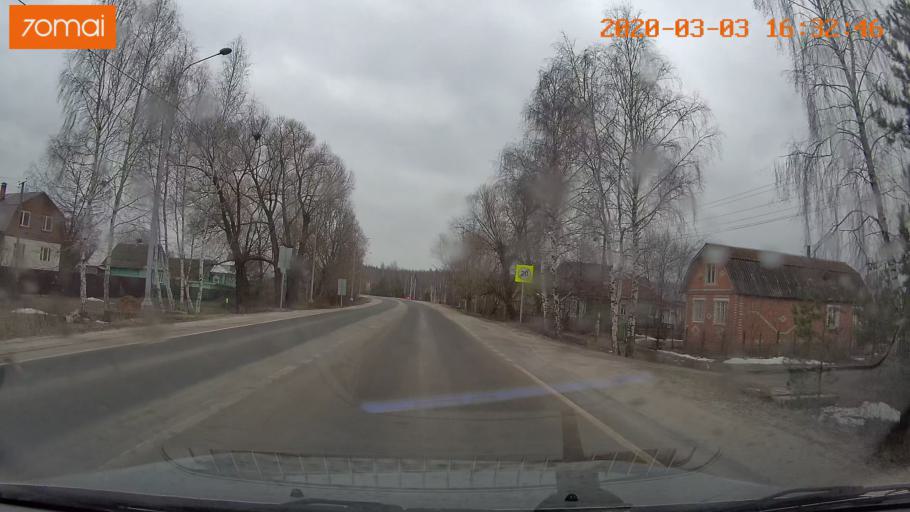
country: RU
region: Moskovskaya
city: Konobeyevo
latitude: 55.4192
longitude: 38.7347
